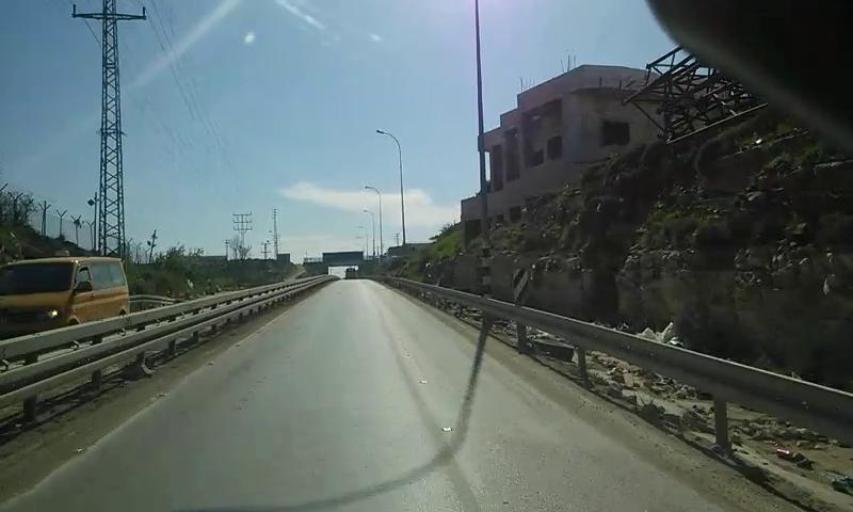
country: PS
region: West Bank
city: Ar Ram wa Dahiyat al Barid
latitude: 31.8549
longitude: 35.2439
